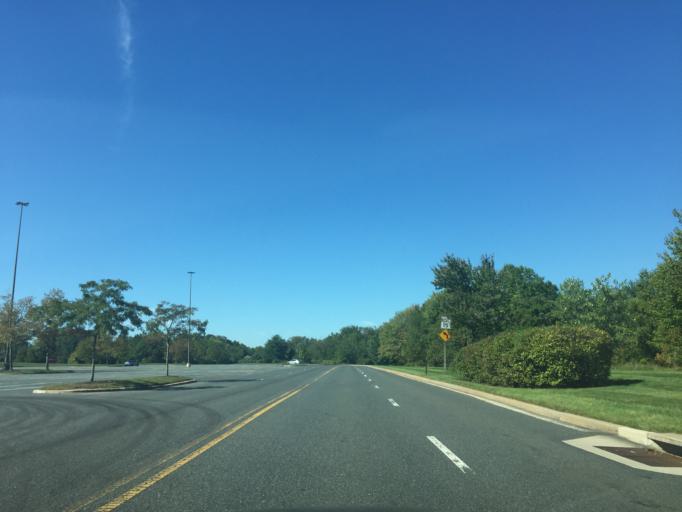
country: US
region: Maryland
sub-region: Baltimore County
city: Perry Hall
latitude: 39.3778
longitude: -76.4674
